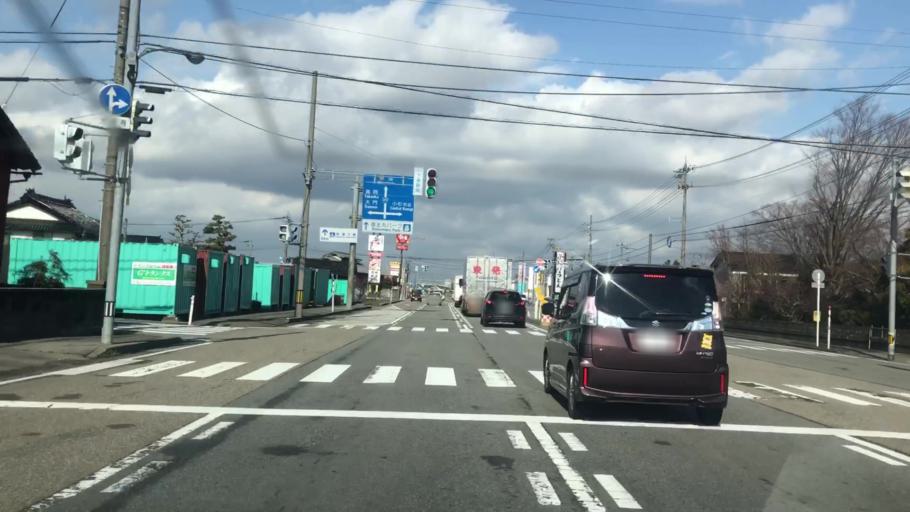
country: JP
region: Toyama
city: Kuragaki-kosugi
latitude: 36.7160
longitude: 137.0816
